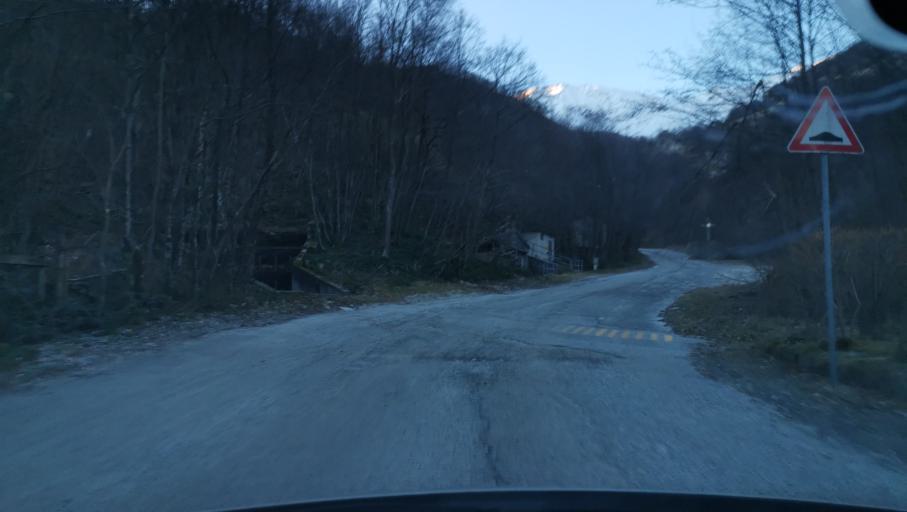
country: IT
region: Piedmont
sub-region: Provincia di Torino
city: Rora
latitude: 44.7697
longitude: 7.2049
